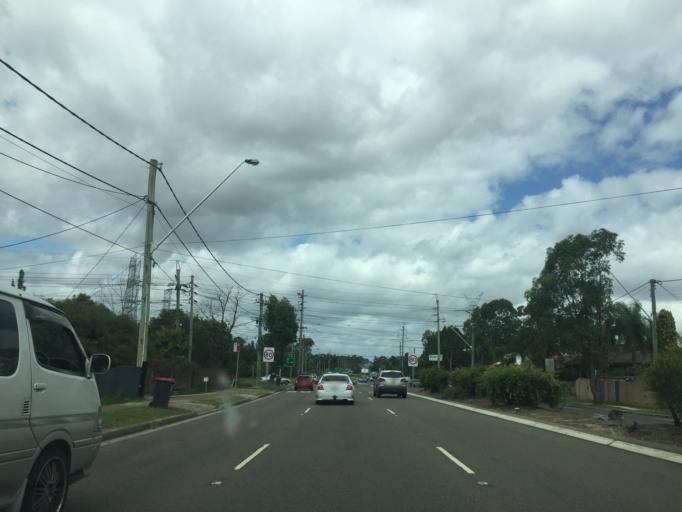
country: AU
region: New South Wales
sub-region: Blacktown
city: Mount Druitt
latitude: -33.7760
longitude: 150.7998
